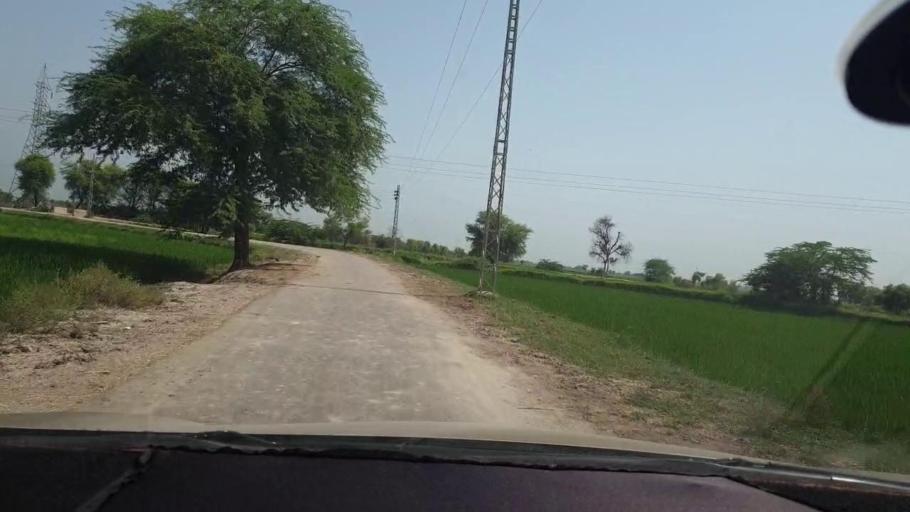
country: PK
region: Sindh
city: Goth Garelo
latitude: 27.4992
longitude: 68.0179
